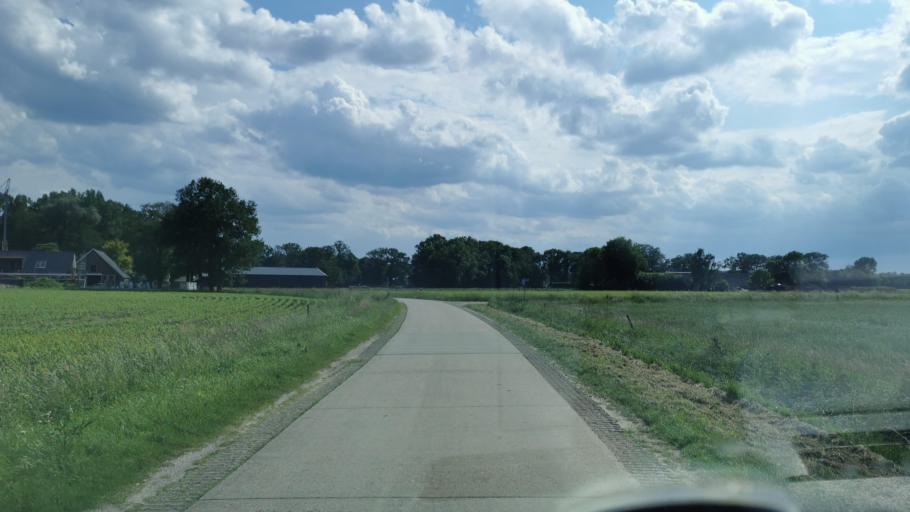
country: NL
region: Overijssel
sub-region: Gemeente Tubbergen
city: Tubbergen
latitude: 52.3432
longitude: 6.8020
